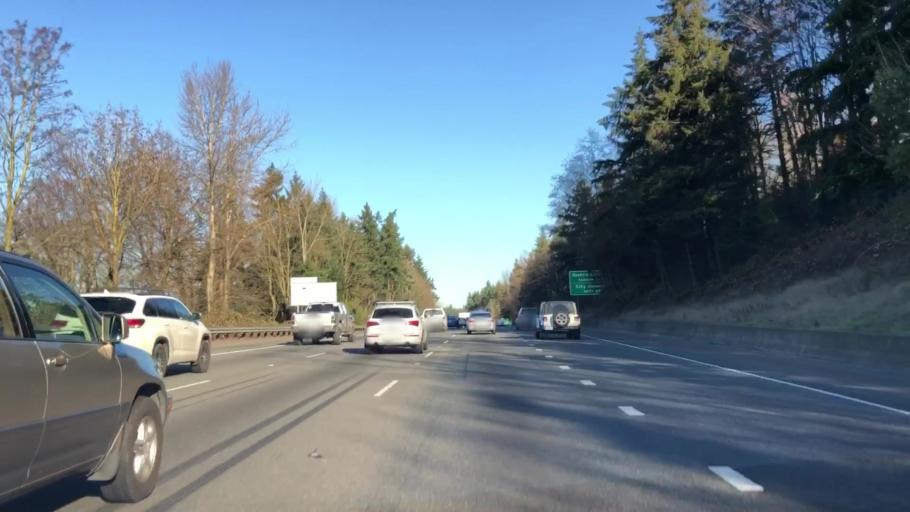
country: US
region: Washington
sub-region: King County
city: Newport
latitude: 47.5938
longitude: -122.1804
